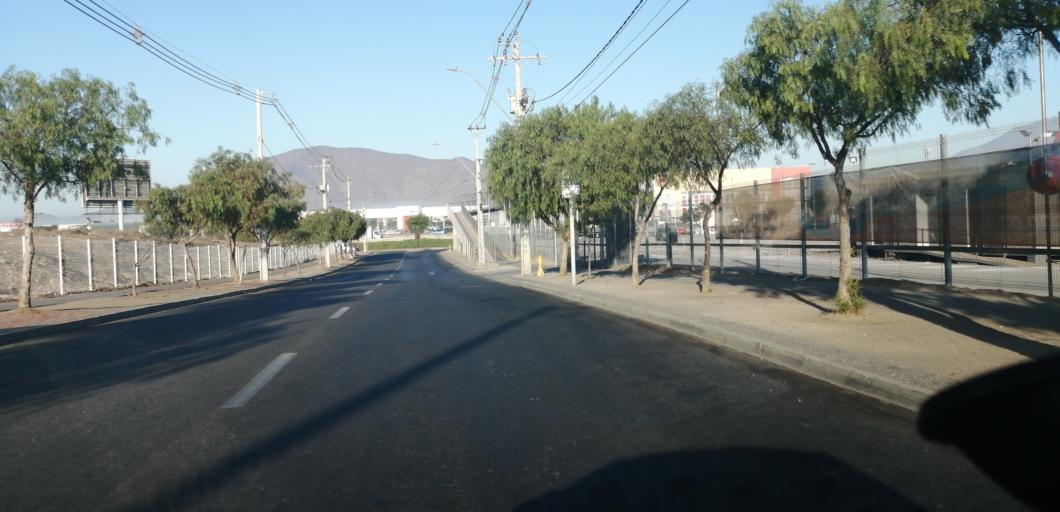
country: CL
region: Santiago Metropolitan
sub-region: Provincia de Santiago
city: Lo Prado
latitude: -33.4351
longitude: -70.7832
